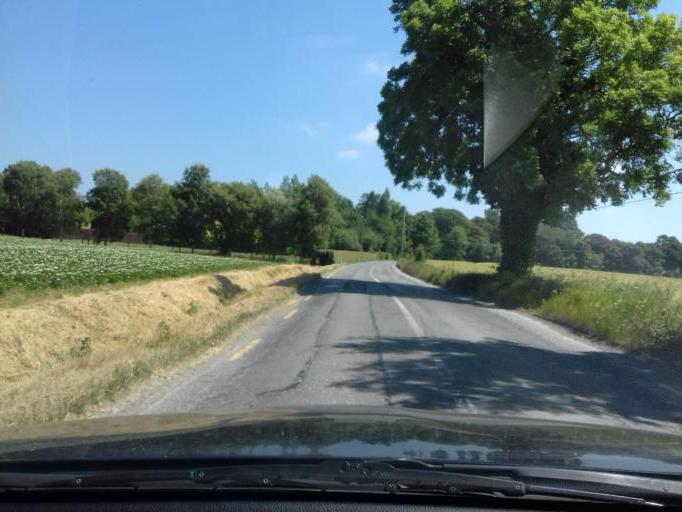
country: IE
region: Leinster
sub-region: Fingal County
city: Swords
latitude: 53.5166
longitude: -6.2490
